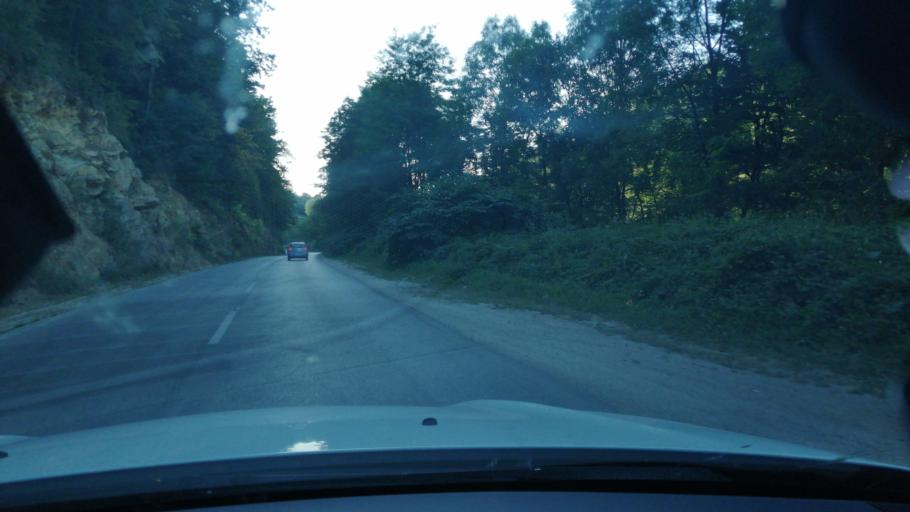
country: RS
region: Central Serbia
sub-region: Moravicki Okrug
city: Lucani
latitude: 43.7610
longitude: 20.2447
